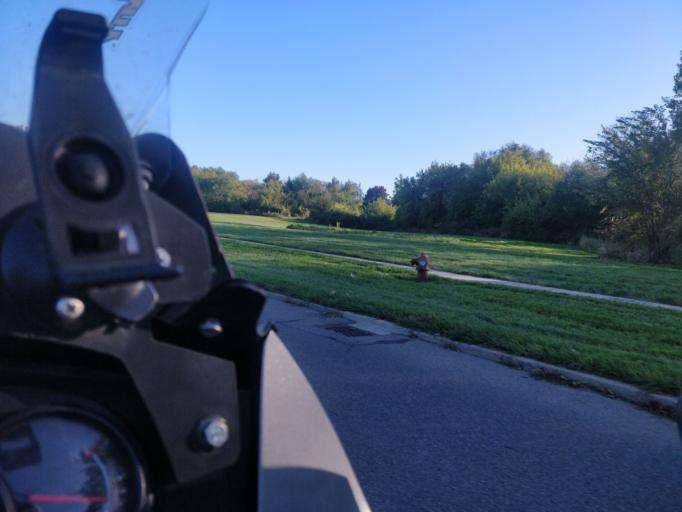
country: US
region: Michigan
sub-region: Wayne County
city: Lincoln Park
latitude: 42.2662
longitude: -83.1756
